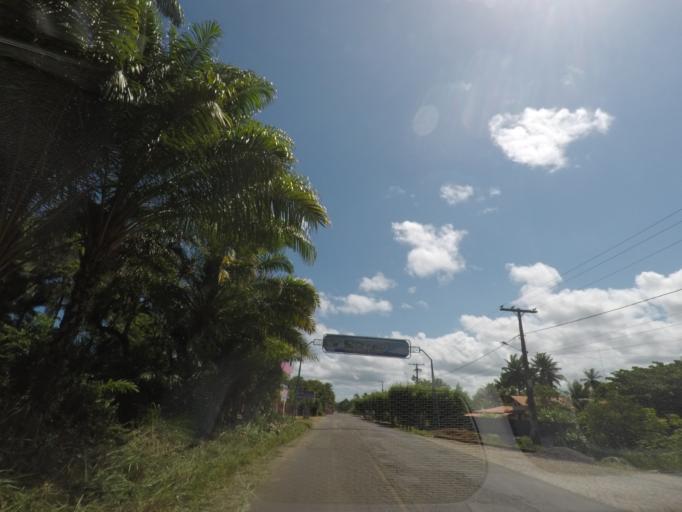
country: BR
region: Bahia
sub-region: Taperoa
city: Taperoa
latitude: -13.4822
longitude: -39.0909
